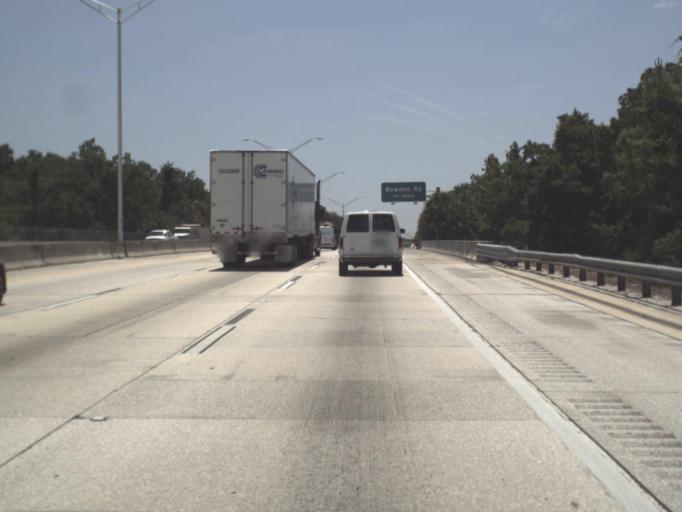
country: US
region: Florida
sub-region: Duval County
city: Jacksonville
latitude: 30.2829
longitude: -81.6220
